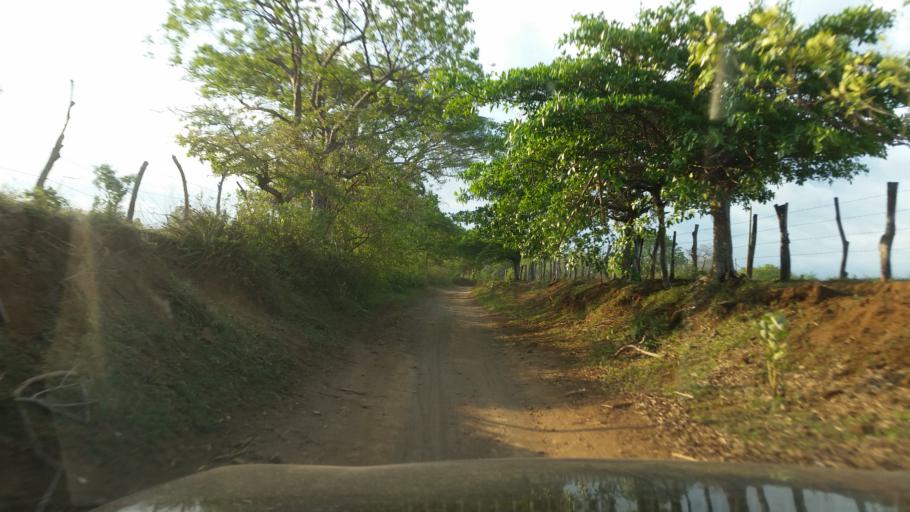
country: NI
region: Managua
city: Masachapa
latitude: 11.7923
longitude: -86.4700
